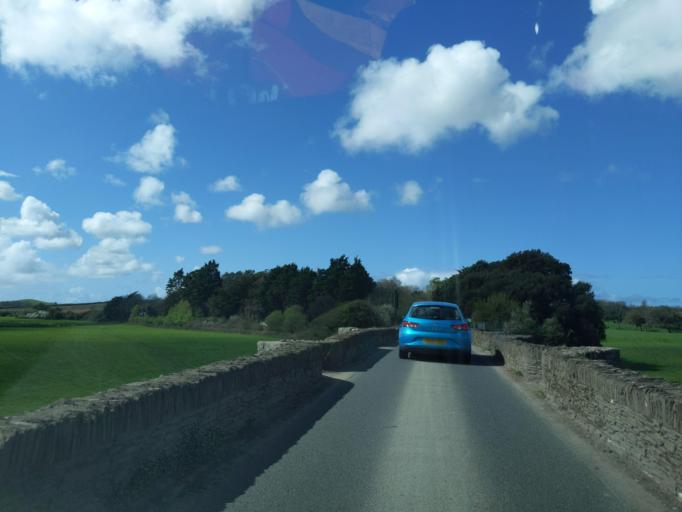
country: GB
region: England
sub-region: Cornwall
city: Wadebridge
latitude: 50.5335
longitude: -4.8411
